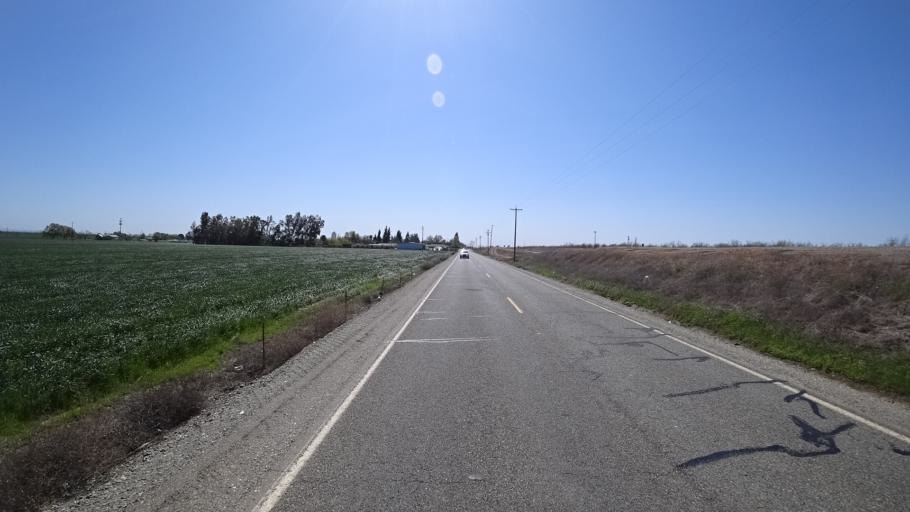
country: US
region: California
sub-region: Glenn County
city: Hamilton City
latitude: 39.7494
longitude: -122.0215
